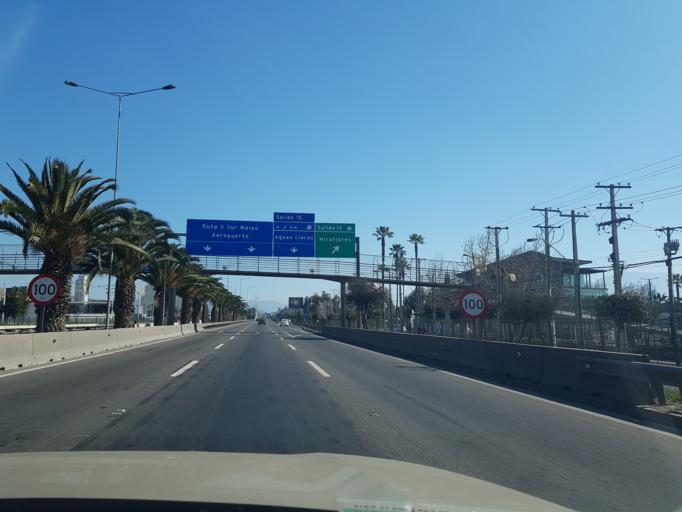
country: CL
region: Santiago Metropolitan
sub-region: Provincia de Santiago
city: Lo Prado
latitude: -33.3902
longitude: -70.7647
